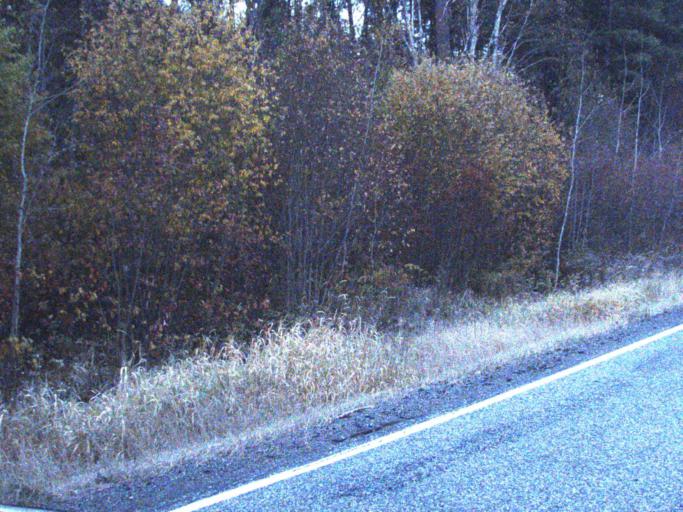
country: US
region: Washington
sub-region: Ferry County
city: Republic
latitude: 48.4256
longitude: -118.7276
